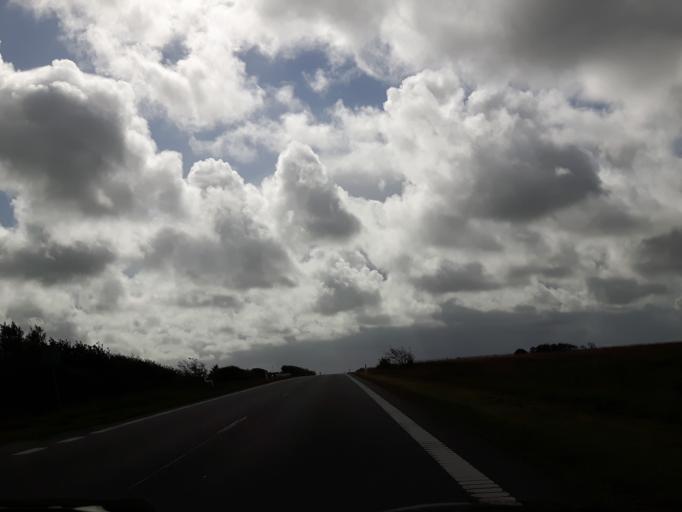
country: DK
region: North Denmark
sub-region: Thisted Kommune
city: Hurup
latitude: 56.7547
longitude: 8.4485
